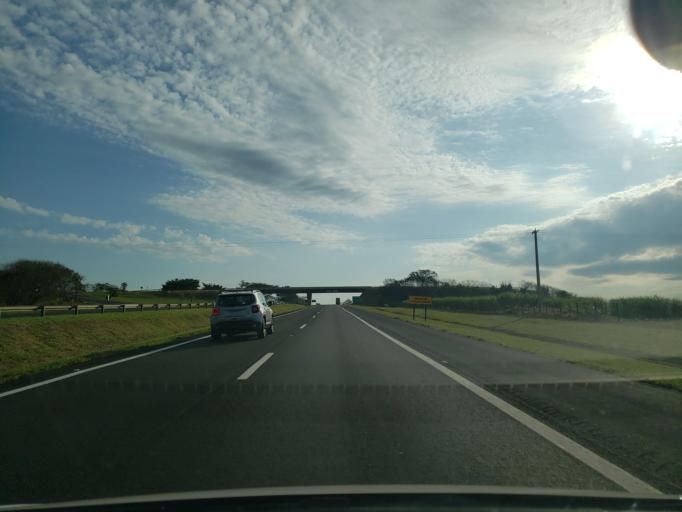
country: BR
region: Sao Paulo
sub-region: Valparaiso
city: Valparaiso
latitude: -21.2051
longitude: -50.7920
